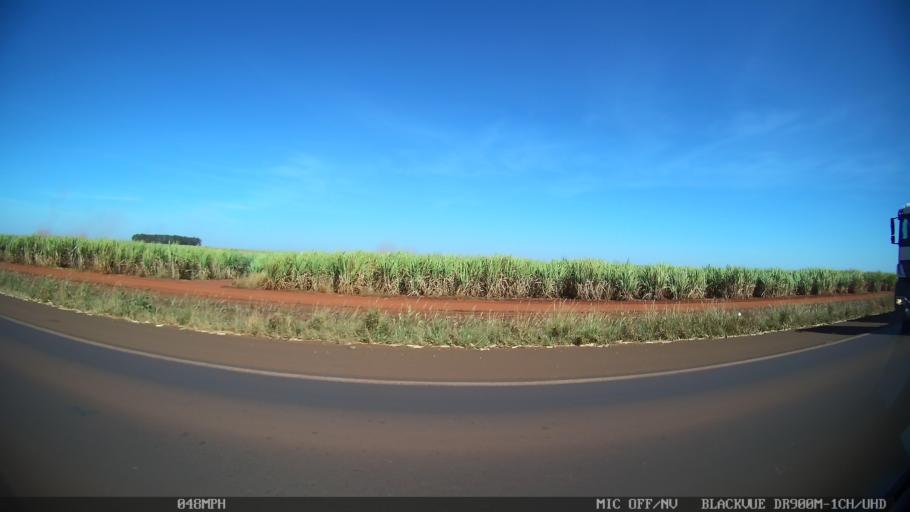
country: BR
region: Sao Paulo
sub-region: Barretos
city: Barretos
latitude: -20.4467
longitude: -48.4422
